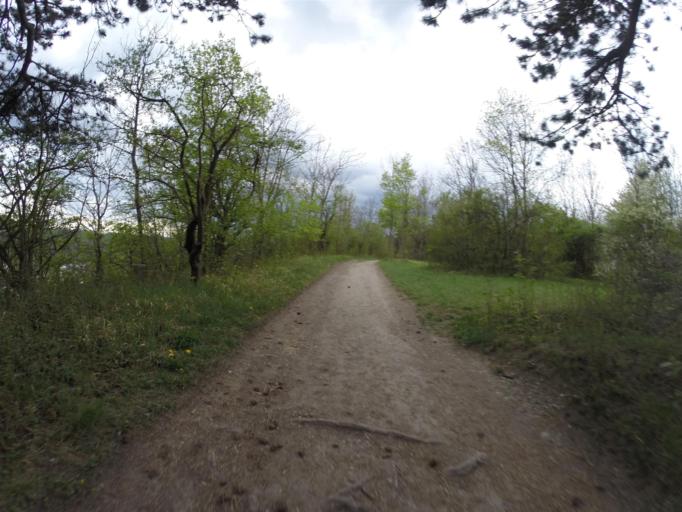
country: DE
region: Thuringia
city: Jena
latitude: 50.9391
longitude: 11.6254
